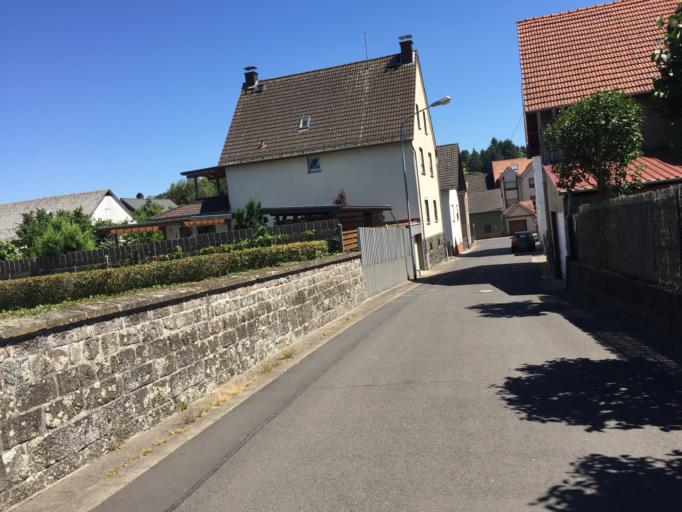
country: DE
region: Hesse
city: Beuern
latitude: 50.6306
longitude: 8.8251
